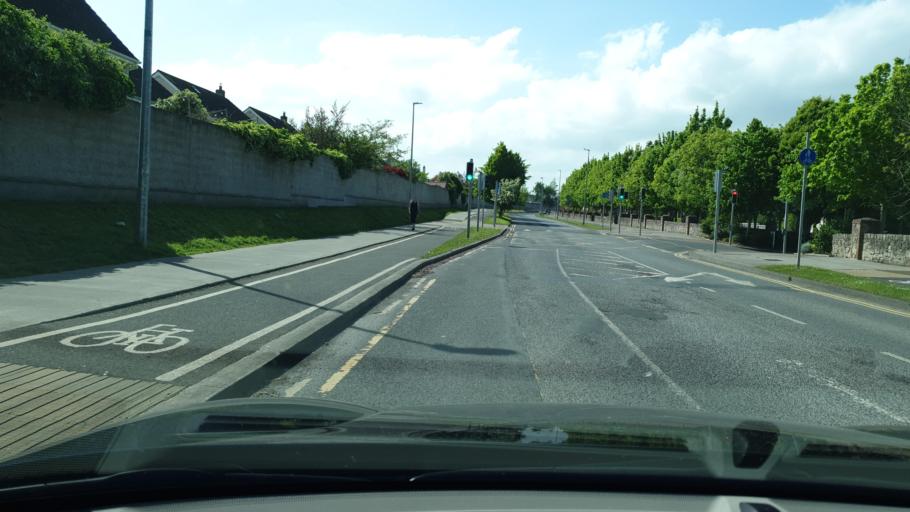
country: IE
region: Leinster
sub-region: An Mhi
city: Ratoath
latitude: 53.5027
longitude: -6.4579
